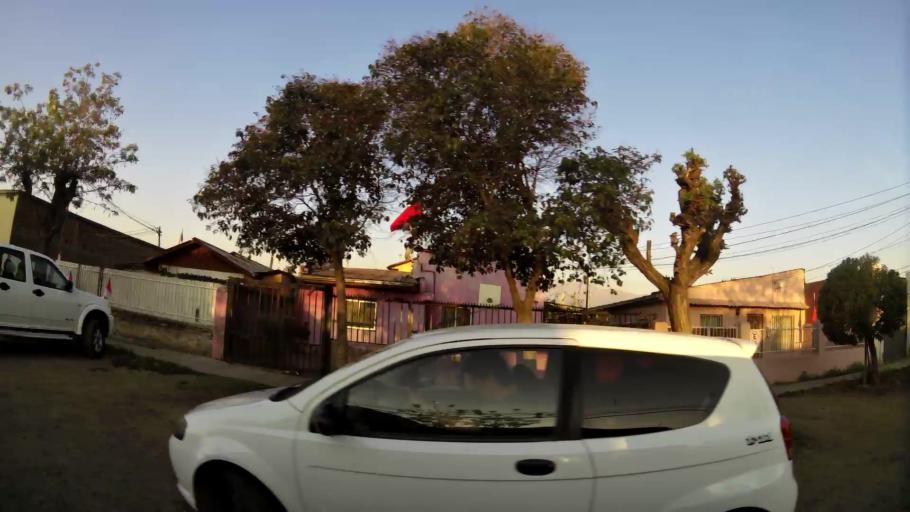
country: CL
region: Santiago Metropolitan
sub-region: Provincia de Santiago
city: Santiago
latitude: -33.5045
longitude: -70.6292
